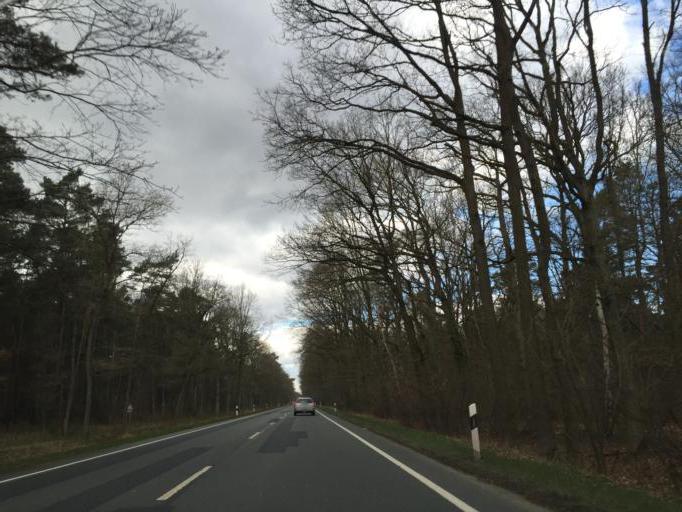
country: DE
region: Lower Saxony
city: Broeckel
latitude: 52.4839
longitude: 10.2564
